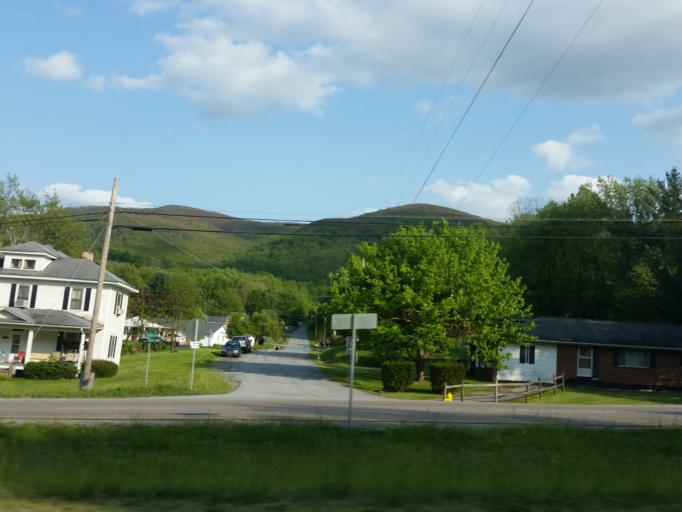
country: US
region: Virginia
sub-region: Tazewell County
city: Springville
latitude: 37.1825
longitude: -81.4292
